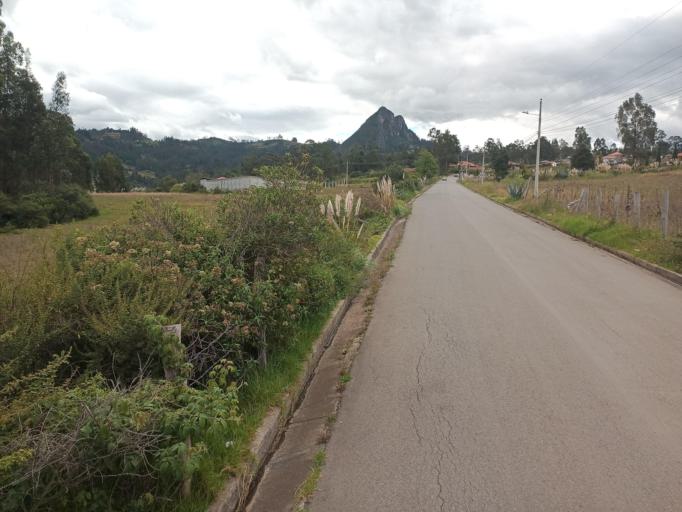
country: EC
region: Canar
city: Azogues
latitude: -2.7820
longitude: -78.8760
